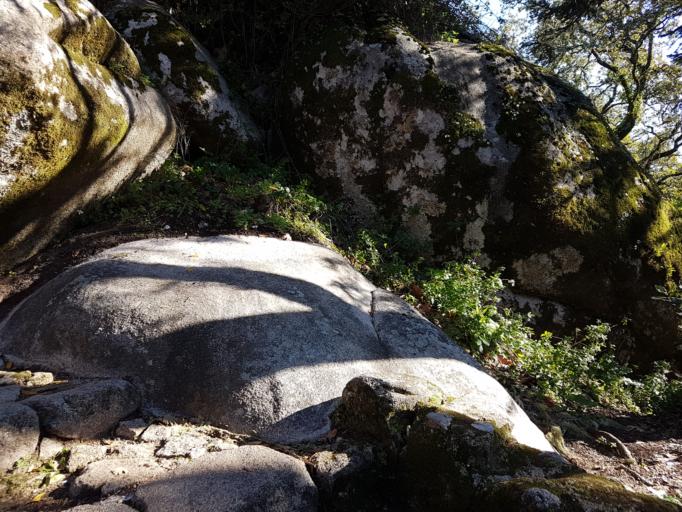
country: PT
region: Lisbon
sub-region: Sintra
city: Sintra
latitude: 38.7929
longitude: -9.3887
